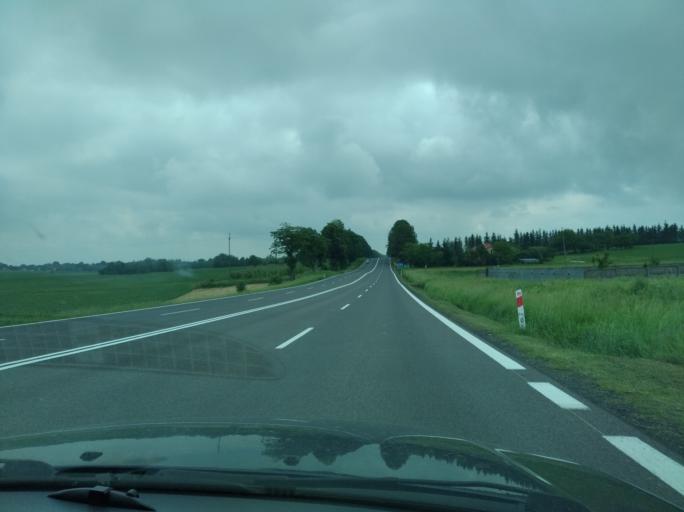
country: PL
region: Subcarpathian Voivodeship
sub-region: Powiat przeworski
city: Nowosielce
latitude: 50.0643
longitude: 22.4274
